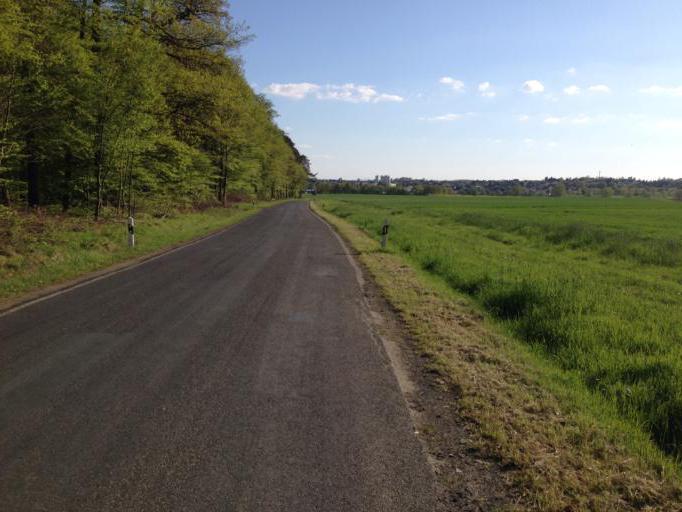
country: DE
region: Hesse
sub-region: Regierungsbezirk Giessen
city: Grossen Buseck
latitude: 50.5640
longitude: 8.7892
